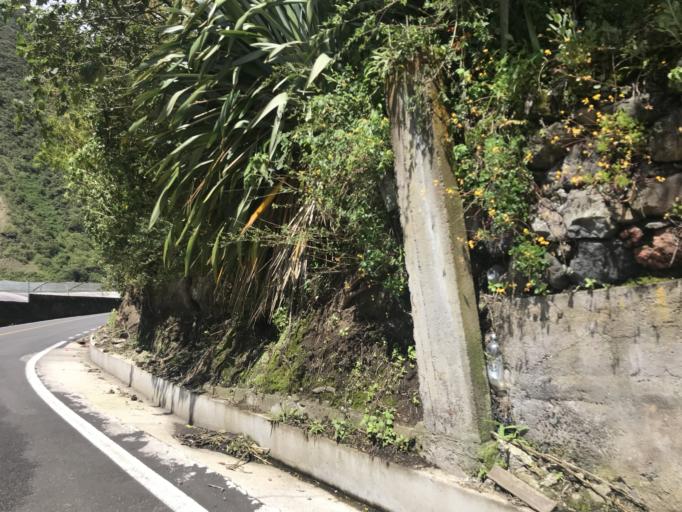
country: EC
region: Tungurahua
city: Banos
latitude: -1.4043
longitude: -78.4057
